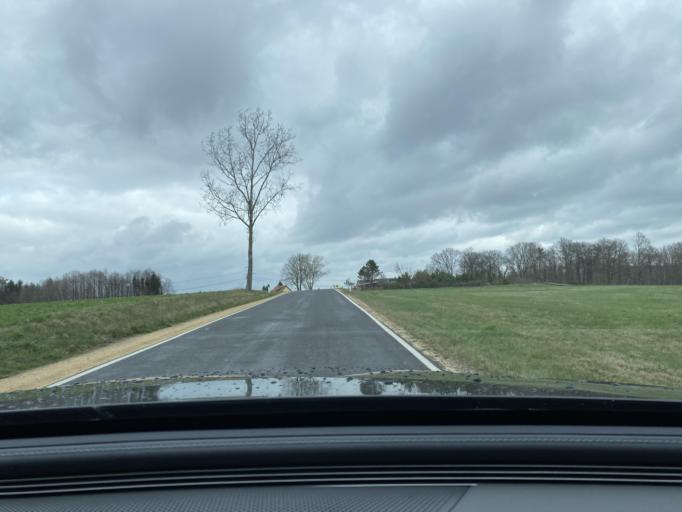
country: DE
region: Saxony
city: Radibor
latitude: 51.2590
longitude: 14.4272
